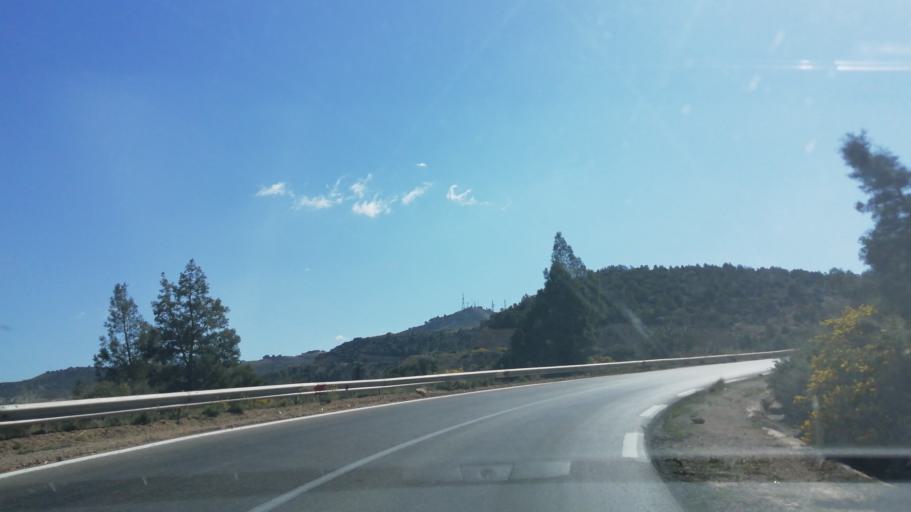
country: DZ
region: Mascara
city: Mascara
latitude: 35.4887
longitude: 0.1505
